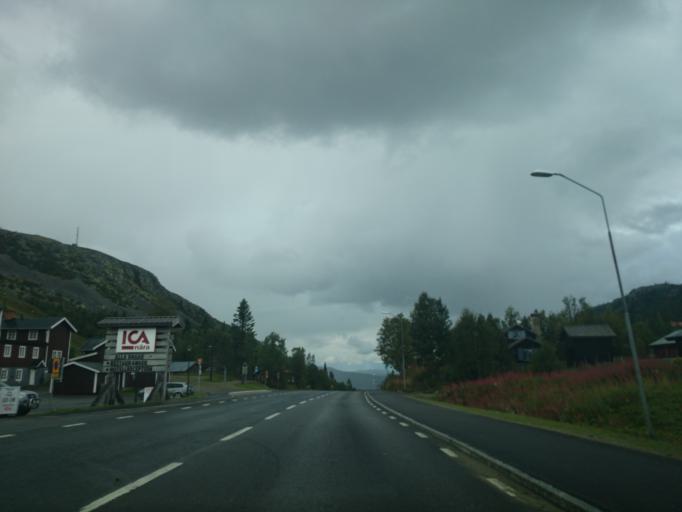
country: SE
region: Jaemtland
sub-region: Bergs Kommun
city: Hoverberg
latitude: 62.4830
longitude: 13.9735
